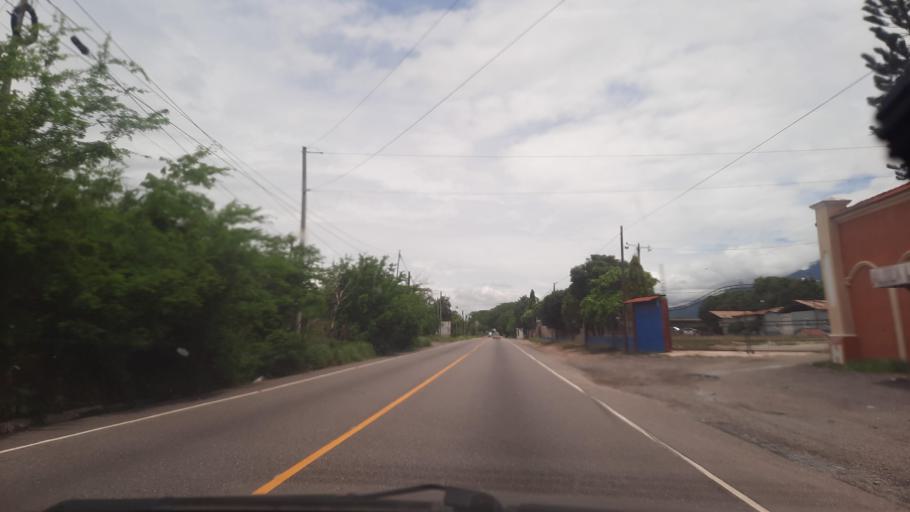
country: GT
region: Zacapa
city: Rio Hondo
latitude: 15.0603
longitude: -89.5405
